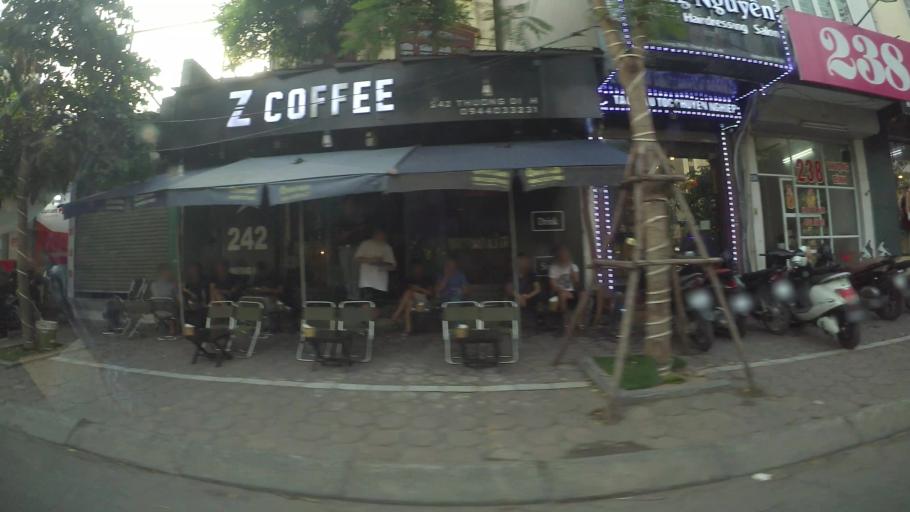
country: VN
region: Ha Noi
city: Thanh Xuan
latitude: 20.9966
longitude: 105.8153
